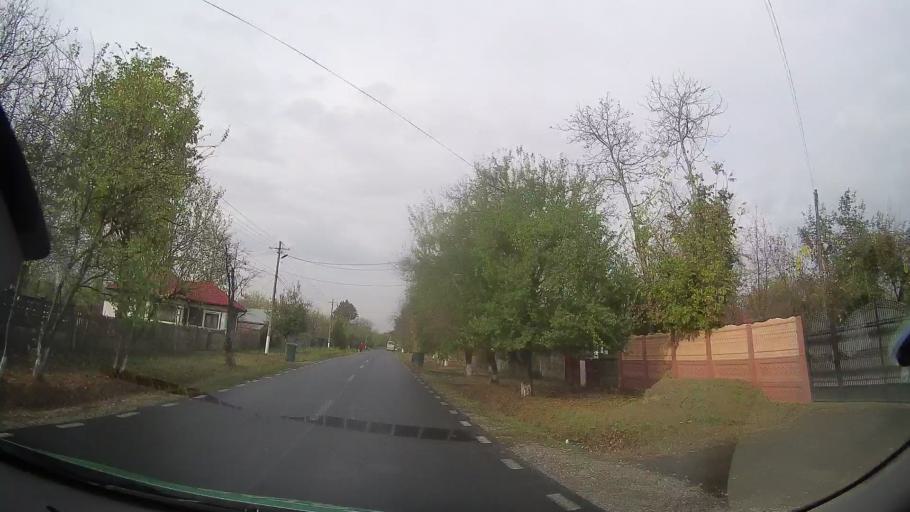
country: RO
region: Ialomita
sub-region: Comuna Fierbinti-Targ
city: Fierbinti-Targ
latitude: 44.7020
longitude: 26.3273
